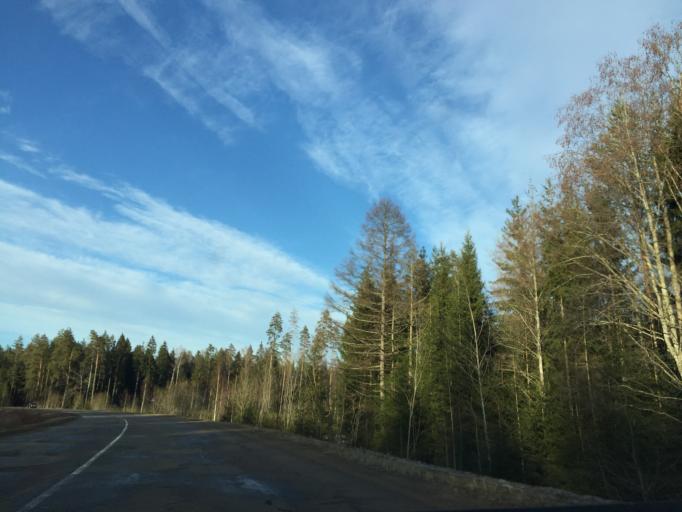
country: LV
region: Kekava
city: Balozi
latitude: 56.7557
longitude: 24.1099
